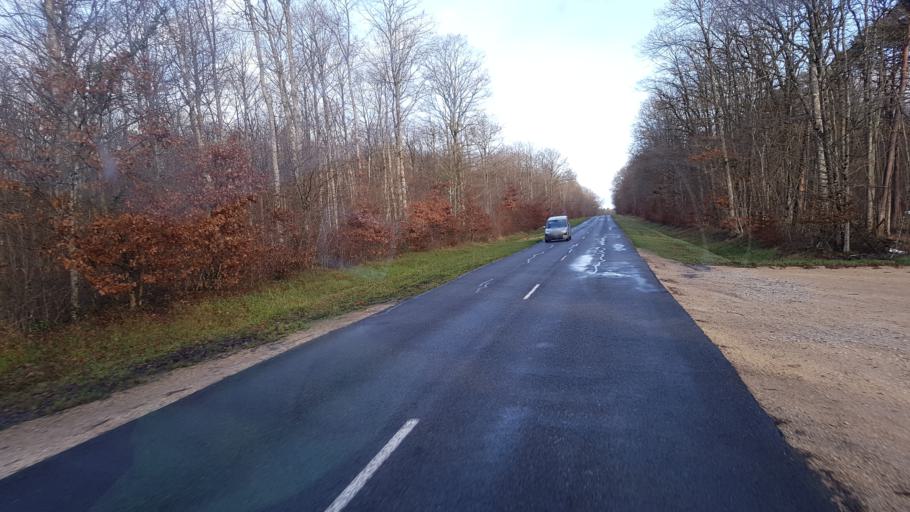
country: FR
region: Centre
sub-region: Departement du Loiret
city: Chilleurs-aux-Bois
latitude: 48.0314
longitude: 2.2109
